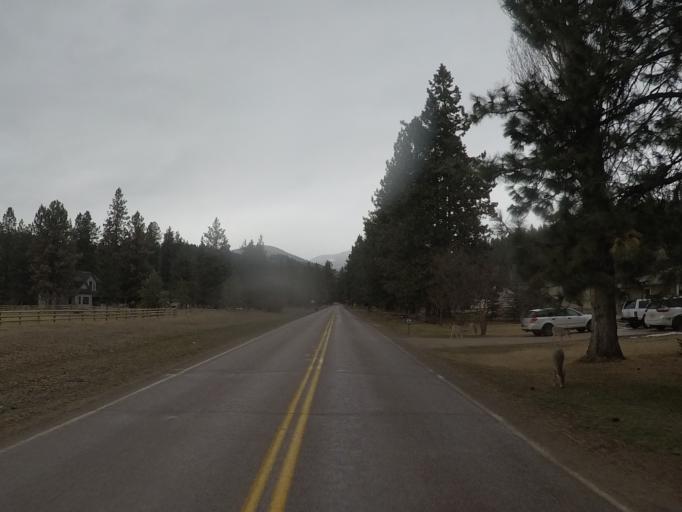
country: US
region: Montana
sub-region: Missoula County
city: East Missoula
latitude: 46.9075
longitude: -113.9604
